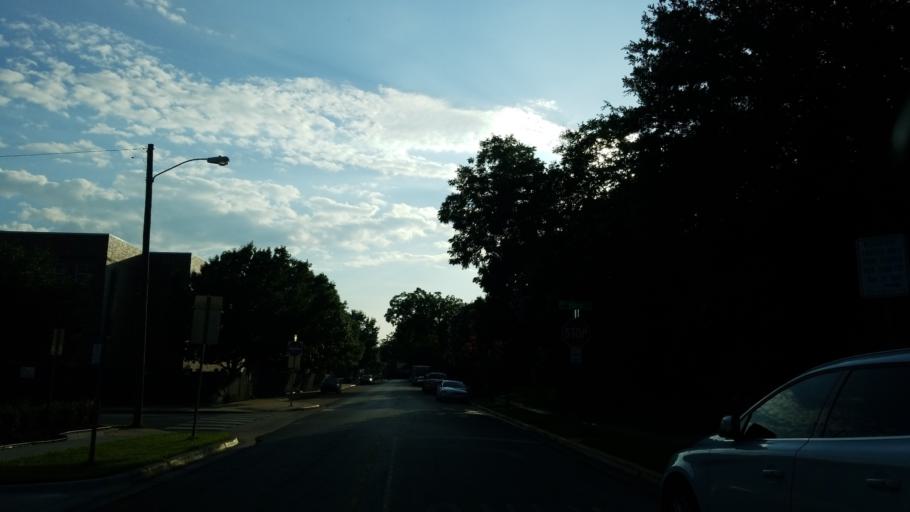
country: US
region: Texas
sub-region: Dallas County
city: Highland Park
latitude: 32.8418
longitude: -96.7892
